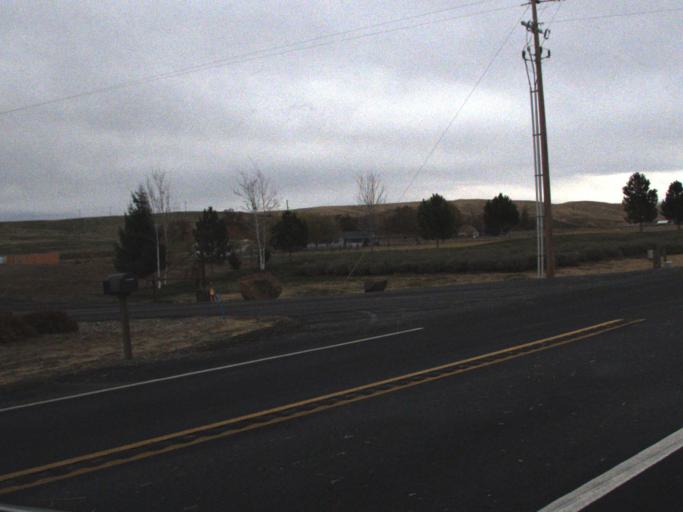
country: US
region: Washington
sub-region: Walla Walla County
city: Garrett
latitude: 46.0530
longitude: -118.5548
